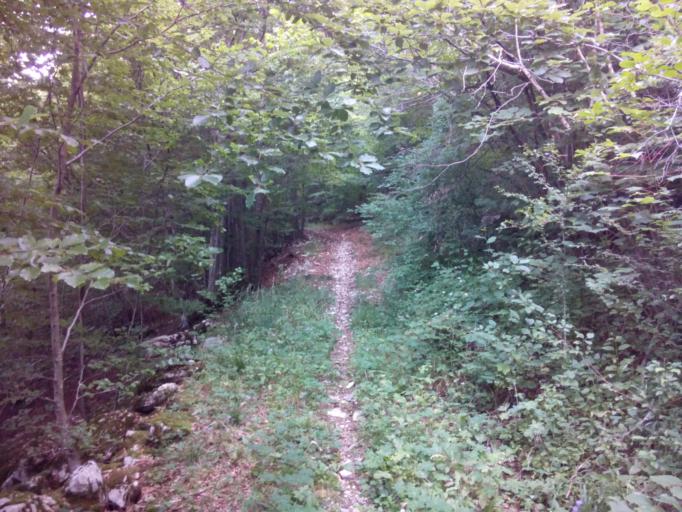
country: IT
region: Veneto
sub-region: Provincia di Vicenza
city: Conco
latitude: 45.8119
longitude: 11.6113
